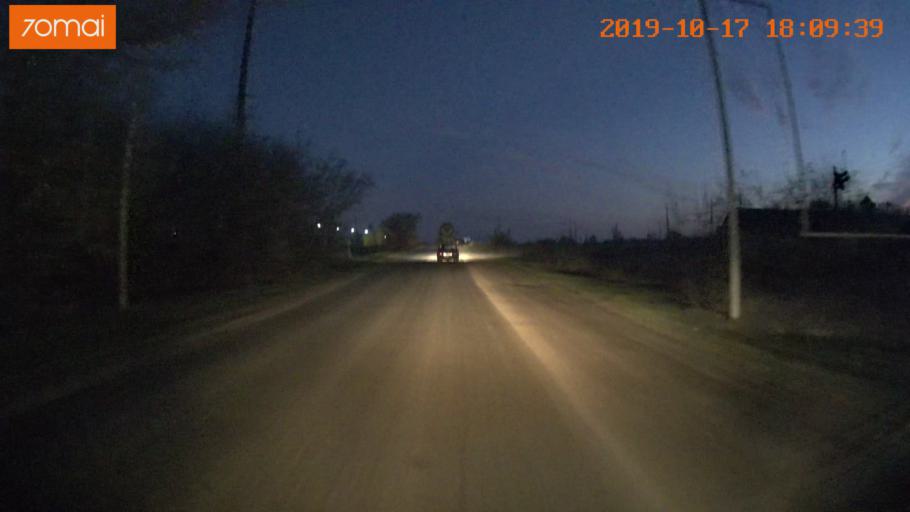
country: RU
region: Tula
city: Kurkino
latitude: 53.4228
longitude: 38.6452
